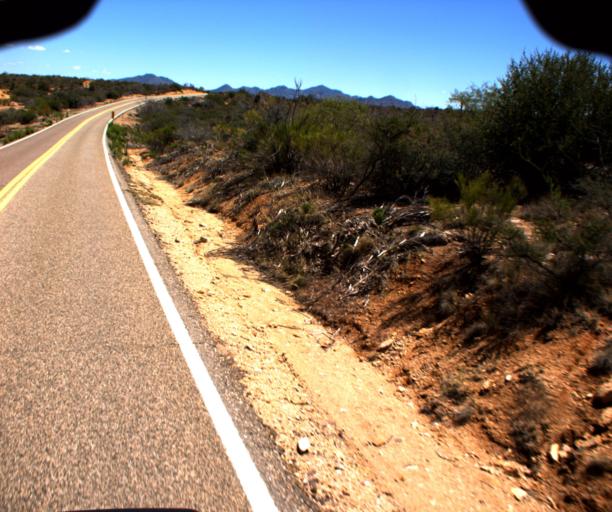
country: US
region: Arizona
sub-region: Yavapai County
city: Bagdad
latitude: 34.4404
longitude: -112.9317
